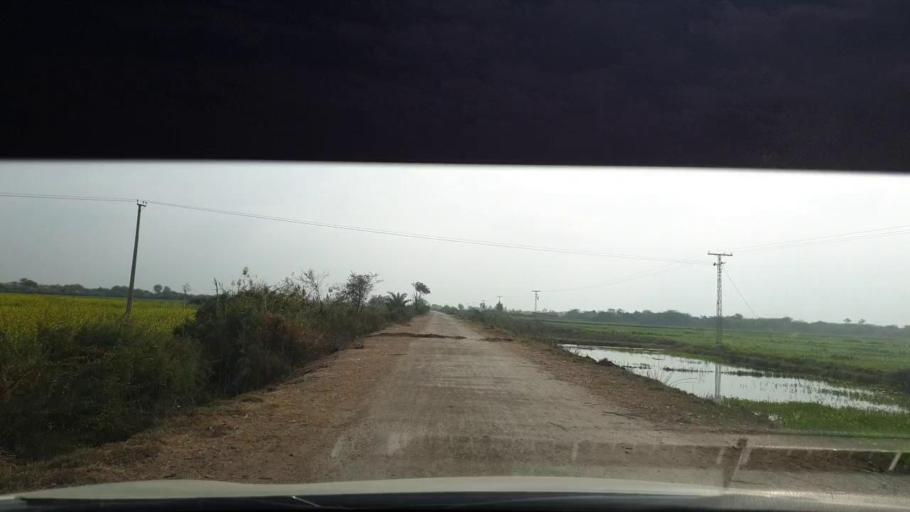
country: PK
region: Sindh
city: Berani
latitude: 25.7688
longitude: 68.8761
